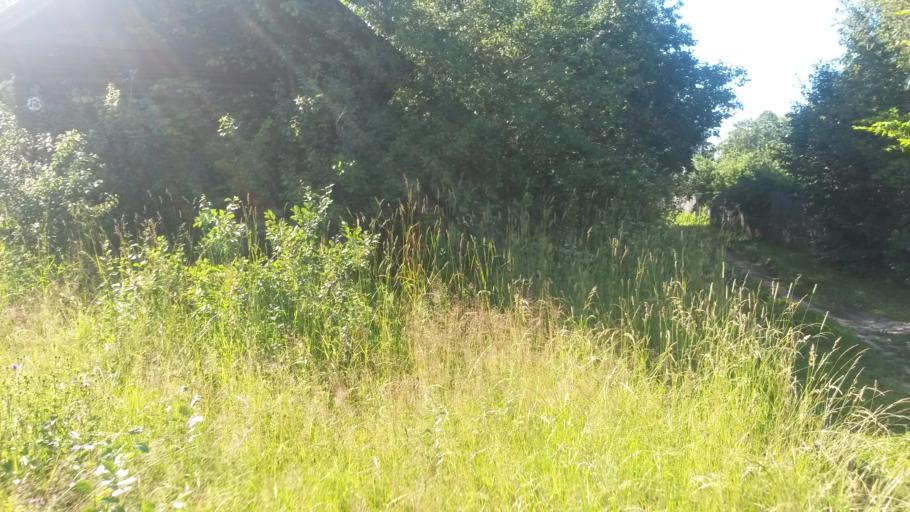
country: RU
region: Ivanovo
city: Zarechnyy
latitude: 57.4959
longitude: 42.3284
